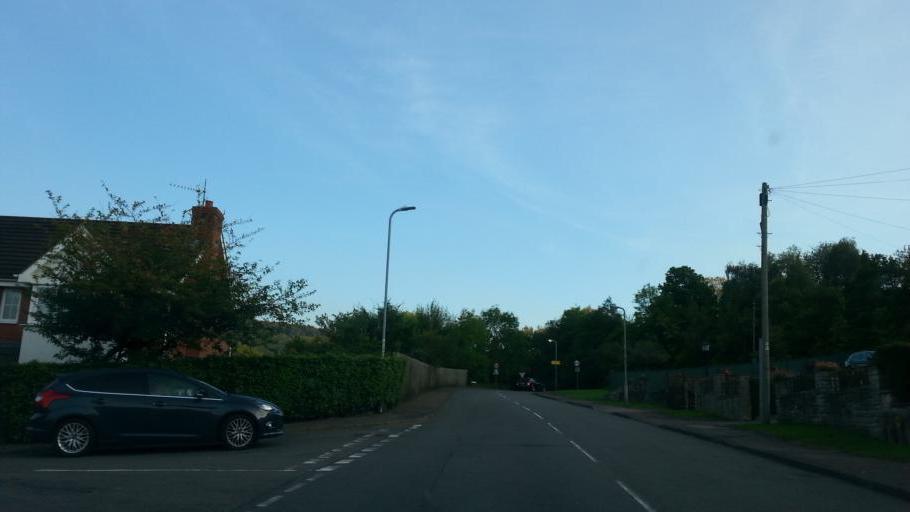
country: GB
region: Wales
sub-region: Monmouthshire
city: Monmouth
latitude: 51.8040
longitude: -2.7150
